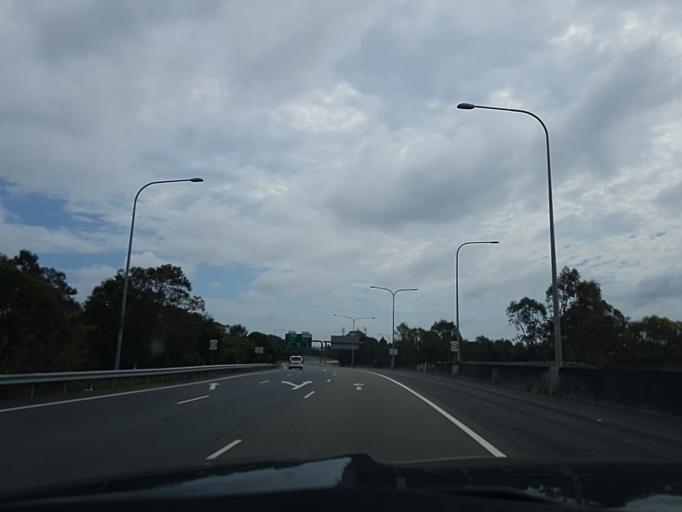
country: AU
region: Queensland
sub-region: Brisbane
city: Cannon Hill
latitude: -27.4559
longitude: 153.1105
